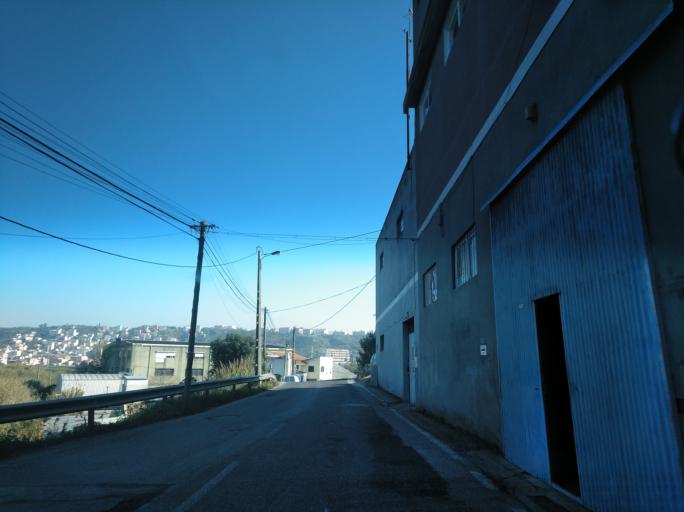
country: PT
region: Lisbon
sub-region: Odivelas
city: Famoes
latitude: 38.7789
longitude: -9.2039
